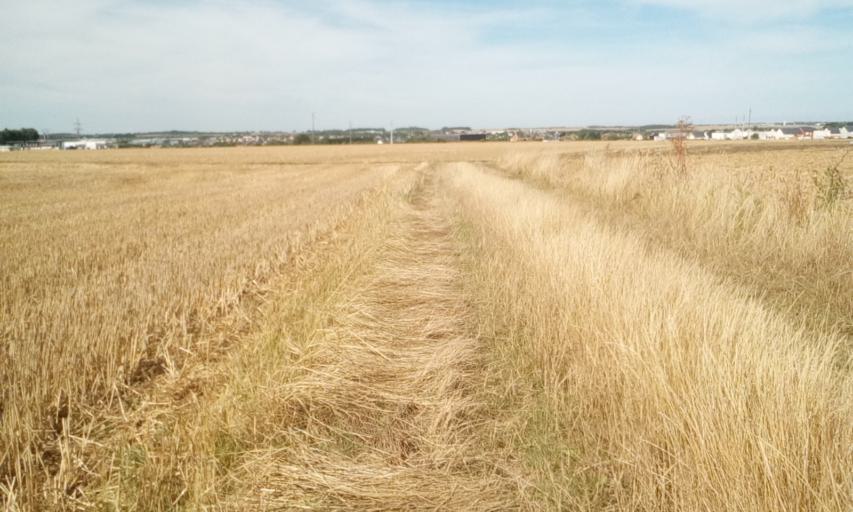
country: FR
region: Lower Normandy
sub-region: Departement du Calvados
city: Fontaine-Etoupefour
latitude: 49.1350
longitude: -0.4553
